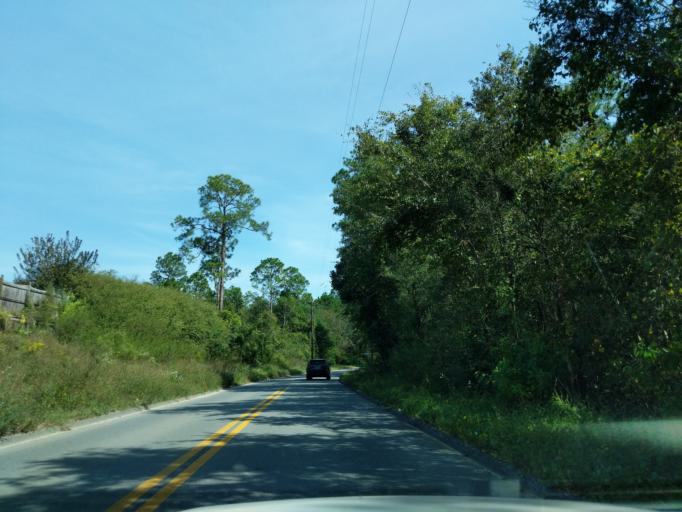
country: US
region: Florida
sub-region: Okaloosa County
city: Crestview
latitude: 30.7037
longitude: -86.5822
